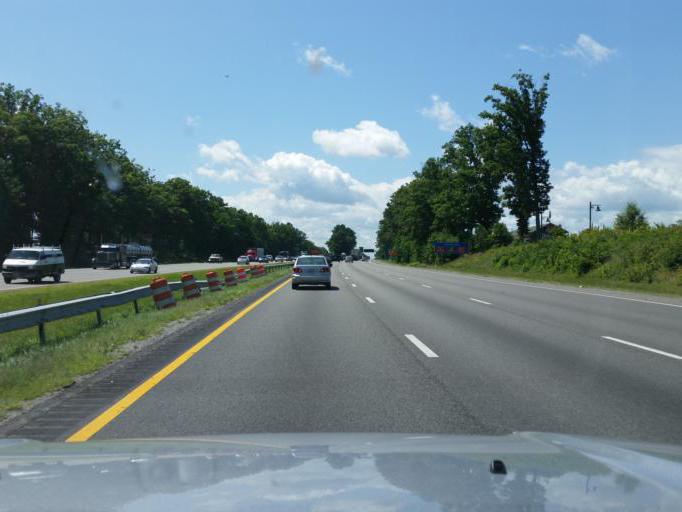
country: US
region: Virginia
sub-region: Hanover County
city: Ashland
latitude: 37.7152
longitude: -77.4480
